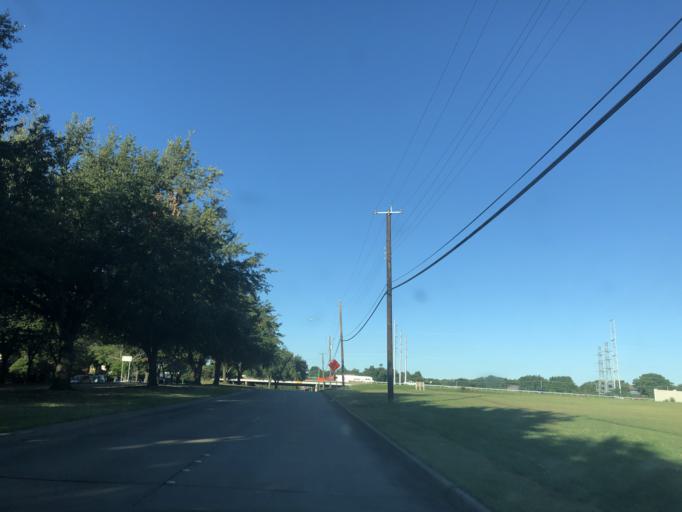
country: US
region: Texas
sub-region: Dallas County
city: Garland
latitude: 32.8456
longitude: -96.6327
